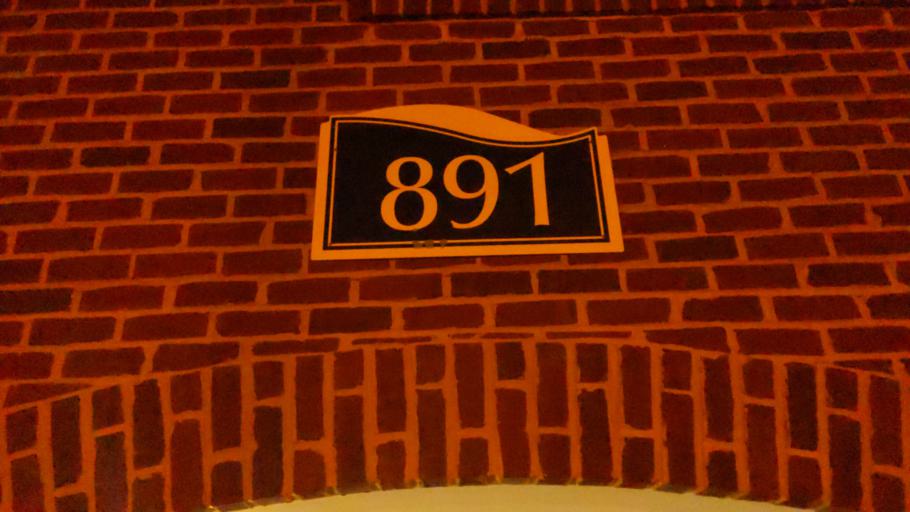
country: US
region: Virginia
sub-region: Montgomery County
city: Merrimac
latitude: 37.1869
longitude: -80.4194
